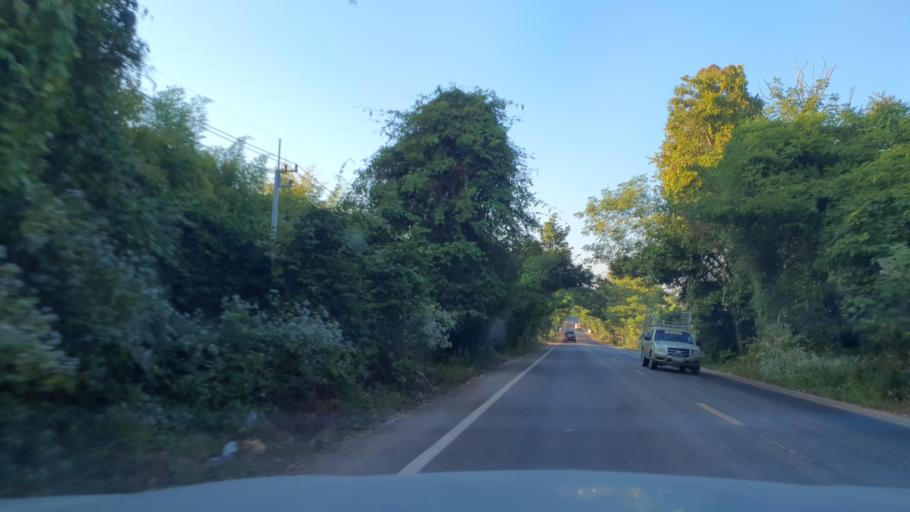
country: TH
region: Nakhon Phanom
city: Si Songkhram
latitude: 17.5642
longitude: 104.2357
